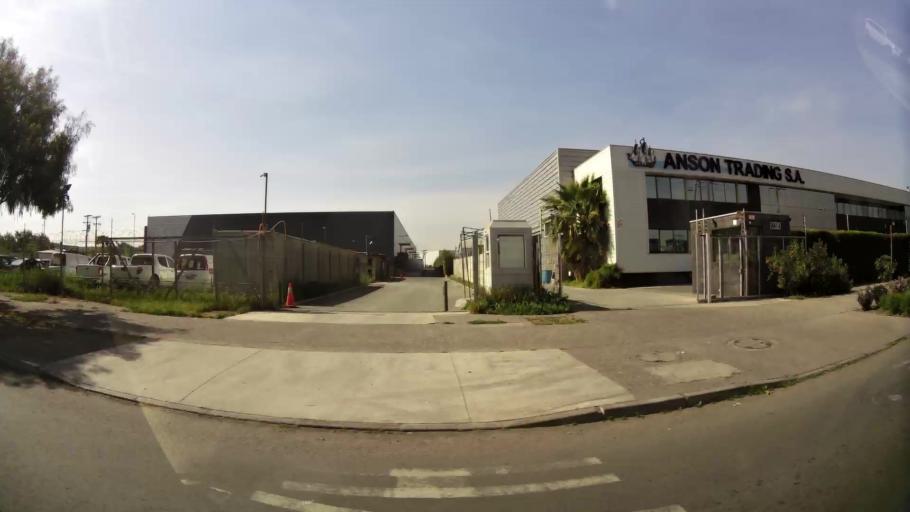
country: CL
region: Santiago Metropolitan
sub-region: Provincia de Santiago
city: Lo Prado
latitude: -33.4298
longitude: -70.7763
